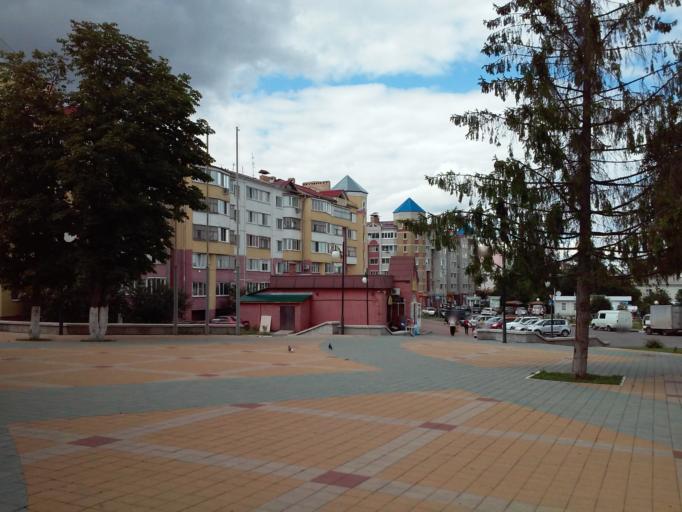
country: RU
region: Belgorod
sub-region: Belgorodskiy Rayon
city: Belgorod
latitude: 50.5368
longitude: 36.5843
